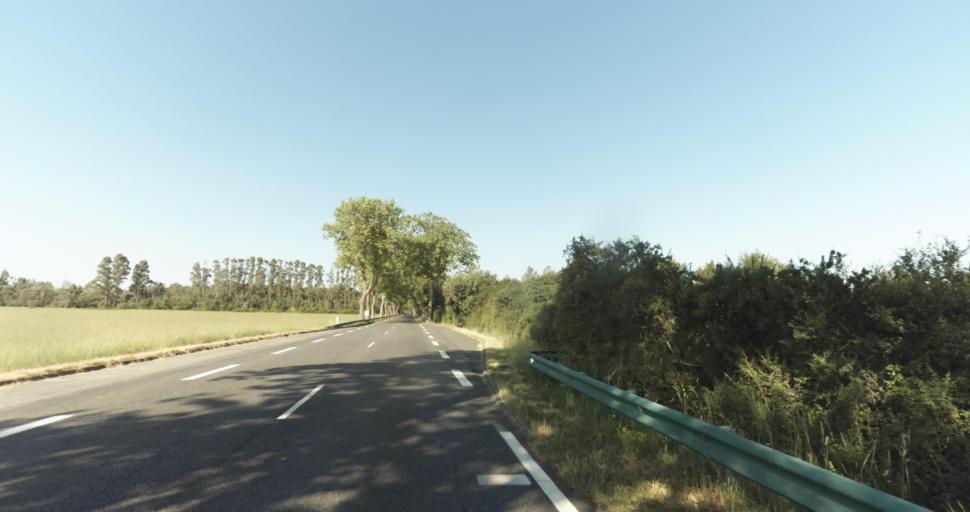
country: FR
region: Midi-Pyrenees
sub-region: Departement de la Haute-Garonne
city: La Salvetat-Saint-Gilles
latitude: 43.5529
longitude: 1.2657
